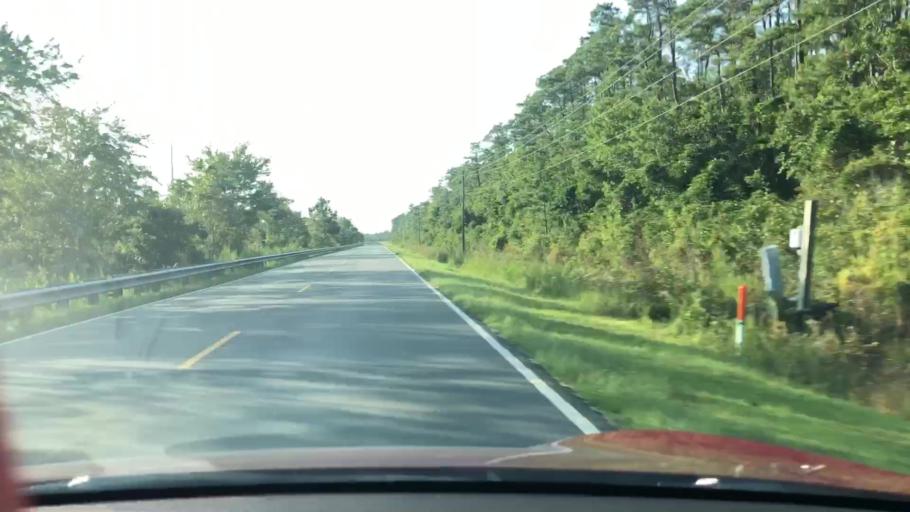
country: US
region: North Carolina
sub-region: Dare County
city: Manteo
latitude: 35.8235
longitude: -75.8027
